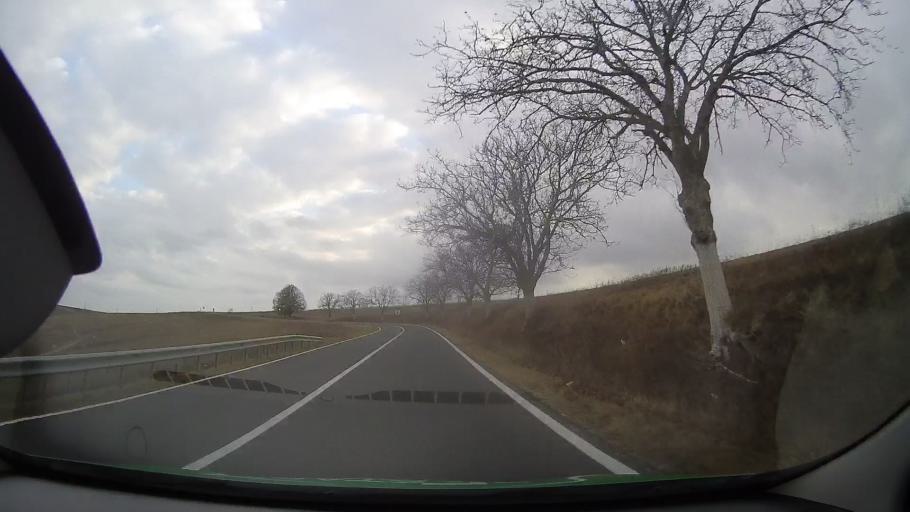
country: RO
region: Constanta
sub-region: Comuna Deleni
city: Deleni
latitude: 44.0962
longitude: 28.0167
